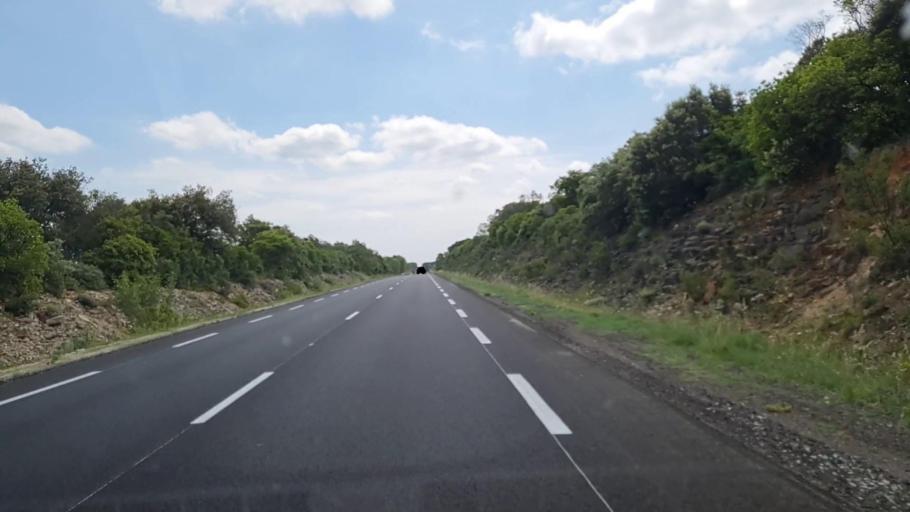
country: FR
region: Languedoc-Roussillon
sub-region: Departement du Gard
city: Clarensac
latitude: 43.8588
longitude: 4.2275
